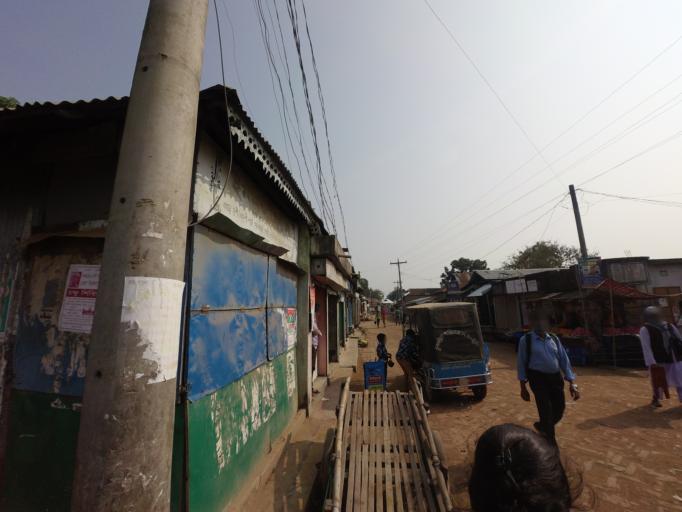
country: BD
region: Dhaka
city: Netrakona
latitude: 25.0106
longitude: 90.6475
